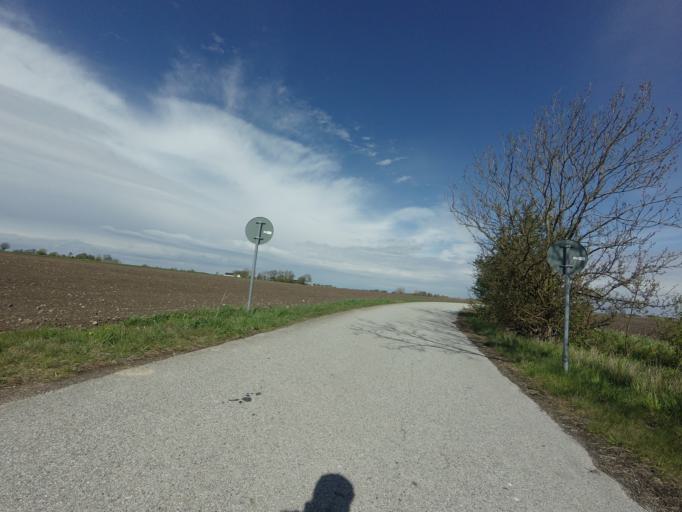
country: SE
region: Skane
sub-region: Malmo
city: Tygelsjo
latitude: 55.5032
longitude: 12.9923
